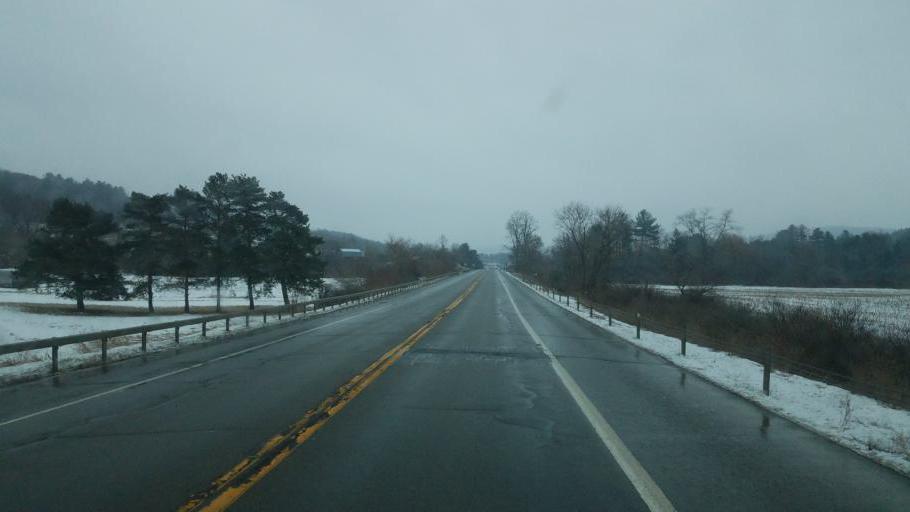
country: US
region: Pennsylvania
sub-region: Tioga County
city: Elkland
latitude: 42.0913
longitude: -77.4200
